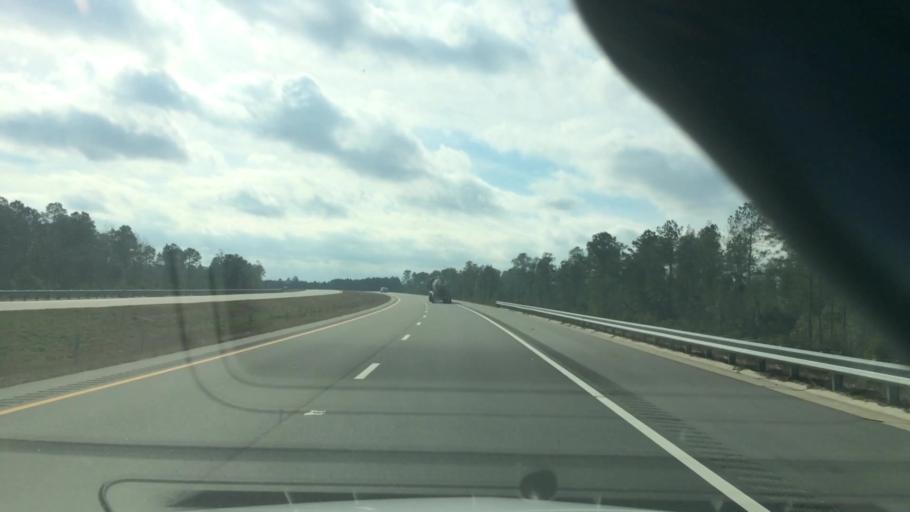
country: US
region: North Carolina
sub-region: Brunswick County
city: Leland
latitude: 34.2758
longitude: -78.0724
